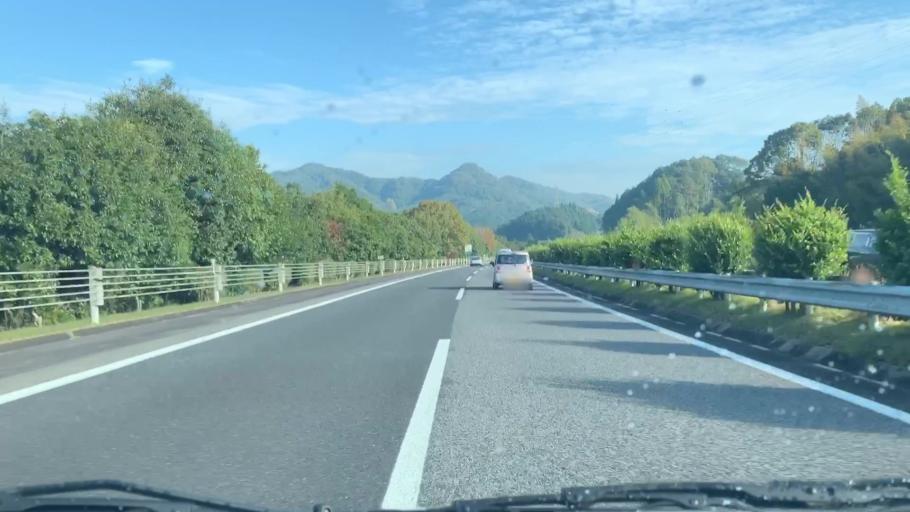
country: JP
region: Saga Prefecture
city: Takeocho-takeo
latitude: 33.2253
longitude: 130.0504
